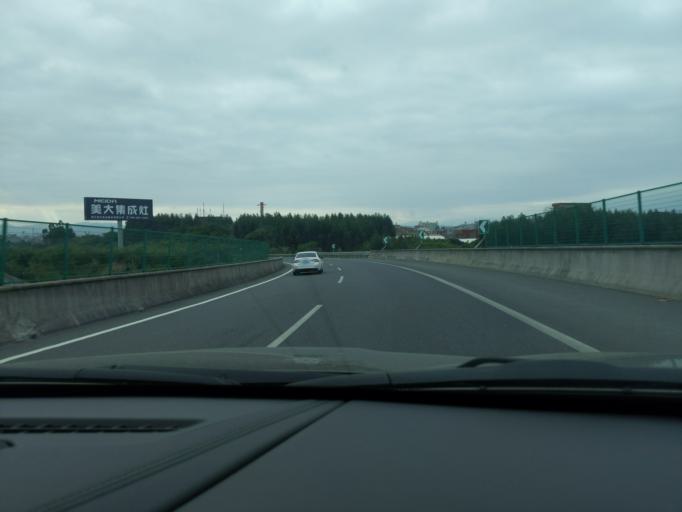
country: CN
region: Fujian
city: Neikeng
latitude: 24.7876
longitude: 118.4773
